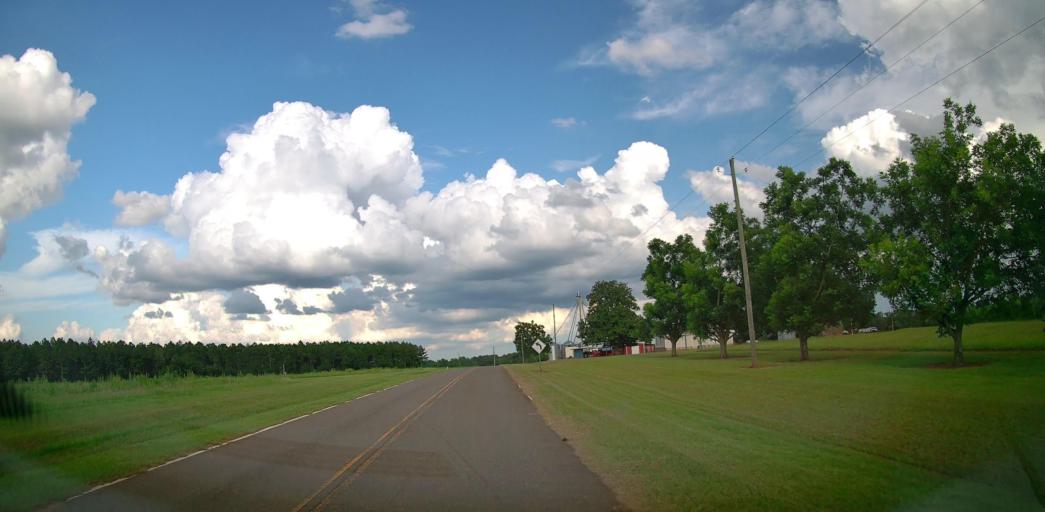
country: US
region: Georgia
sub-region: Bleckley County
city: Cochran
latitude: 32.4135
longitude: -83.4489
